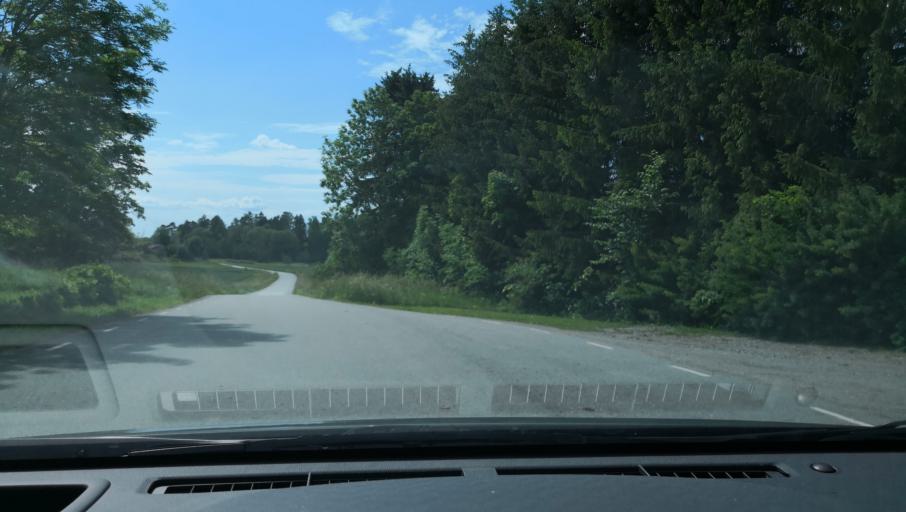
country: SE
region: Uppsala
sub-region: Habo Kommun
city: Balsta
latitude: 59.6918
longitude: 17.4686
